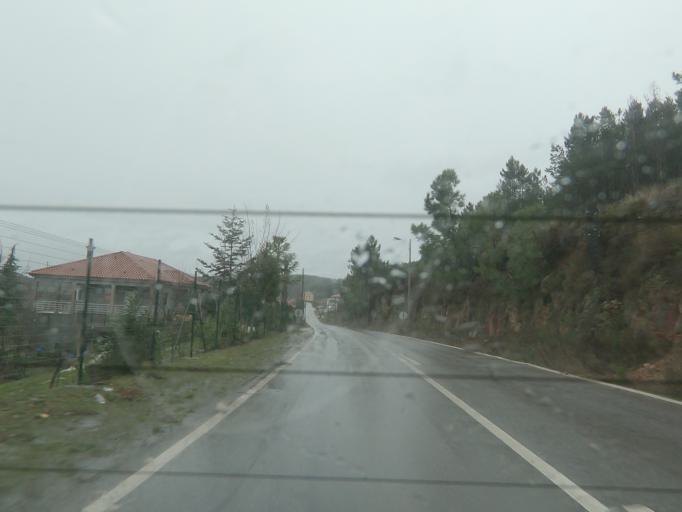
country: PT
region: Vila Real
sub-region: Sabrosa
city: Vilela
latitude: 41.2156
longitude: -7.6748
